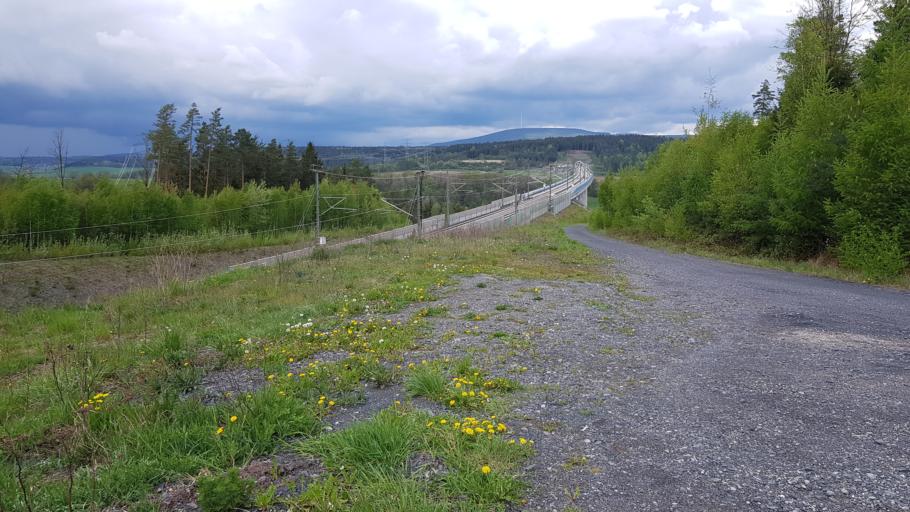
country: DE
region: Thuringia
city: Schalkau
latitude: 50.3831
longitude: 11.0365
